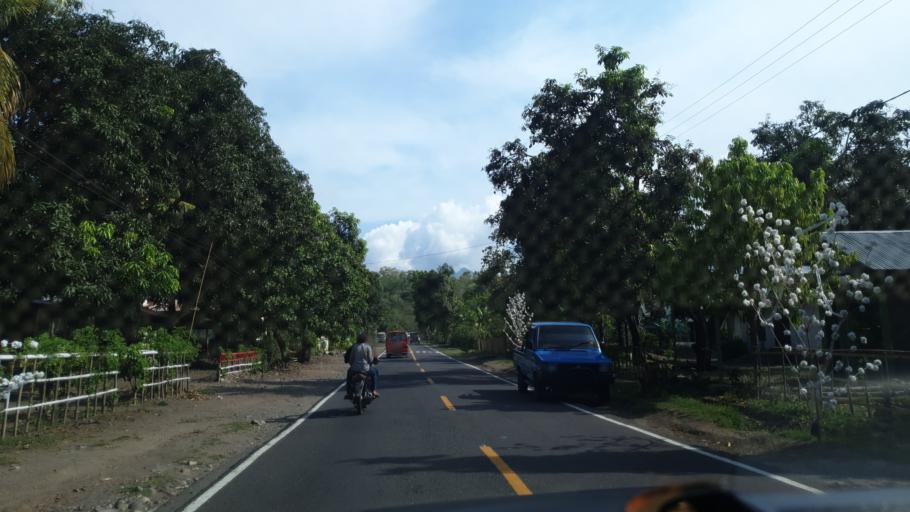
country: ID
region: East Nusa Tenggara
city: Nangalimang
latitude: -8.6513
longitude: 122.2049
